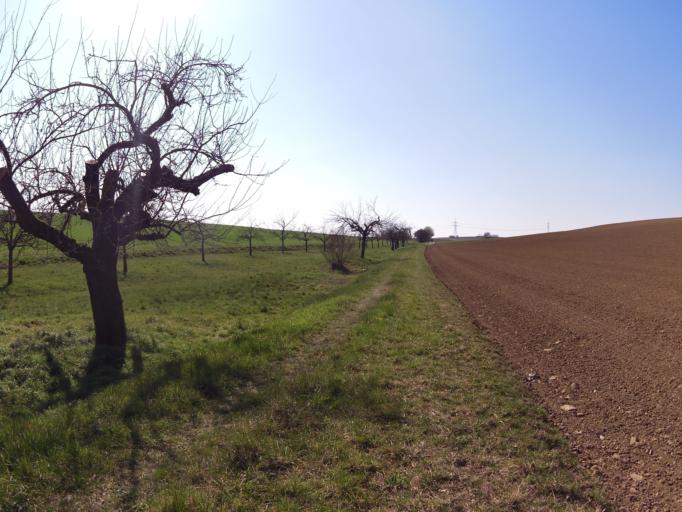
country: DE
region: Bavaria
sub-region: Regierungsbezirk Unterfranken
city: Biebelried
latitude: 49.8167
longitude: 10.1054
